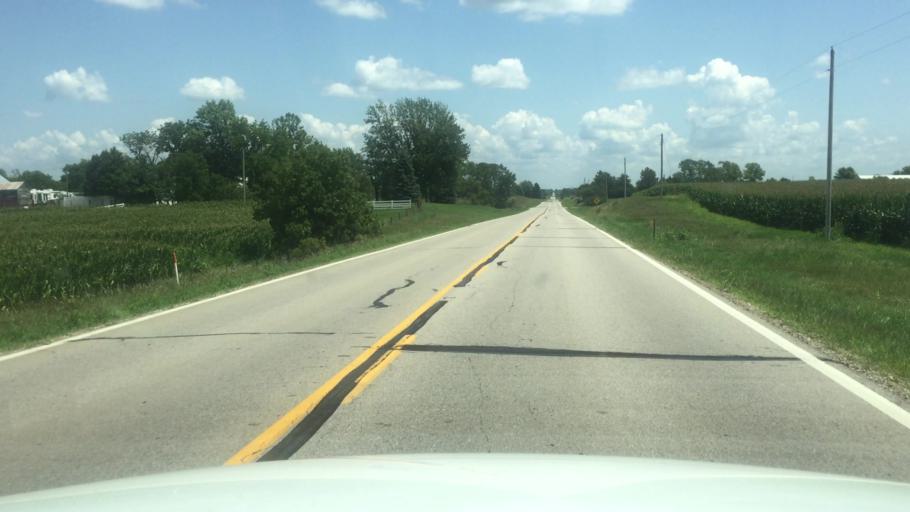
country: US
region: Kansas
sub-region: Brown County
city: Horton
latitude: 39.6674
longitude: -95.5854
